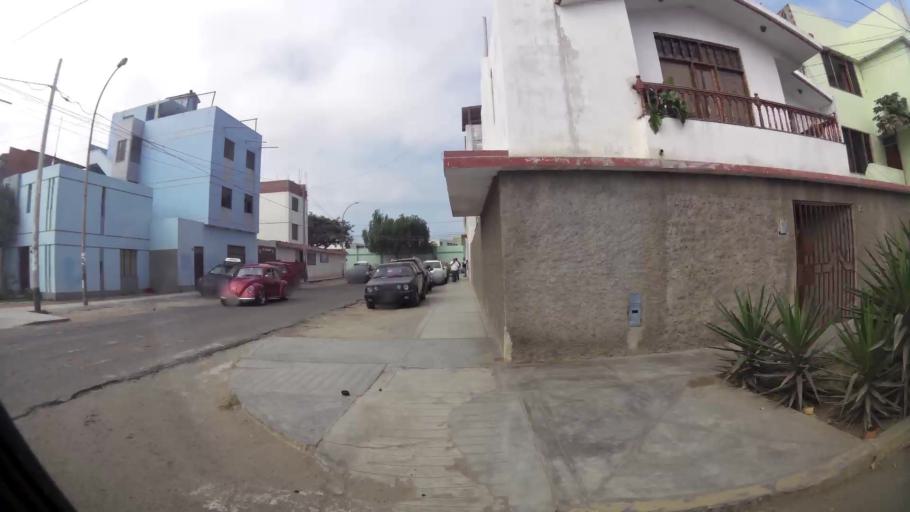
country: PE
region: La Libertad
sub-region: Provincia de Trujillo
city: Trujillo
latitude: -8.1180
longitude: -79.0204
